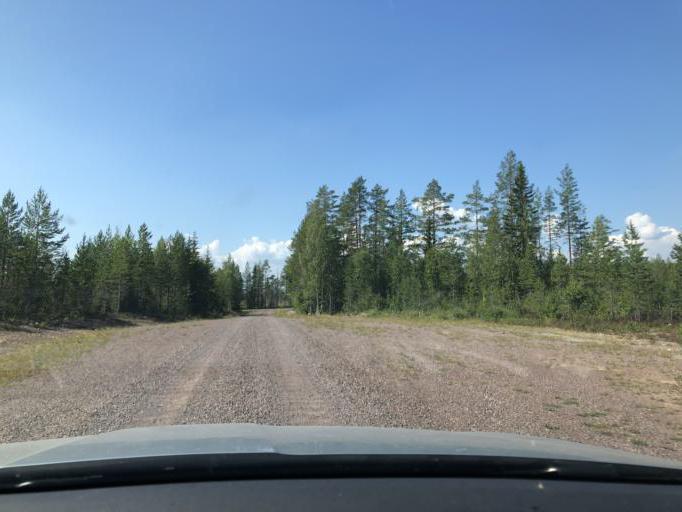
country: SE
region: Dalarna
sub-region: Orsa Kommun
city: Orsa
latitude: 61.2662
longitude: 14.7405
